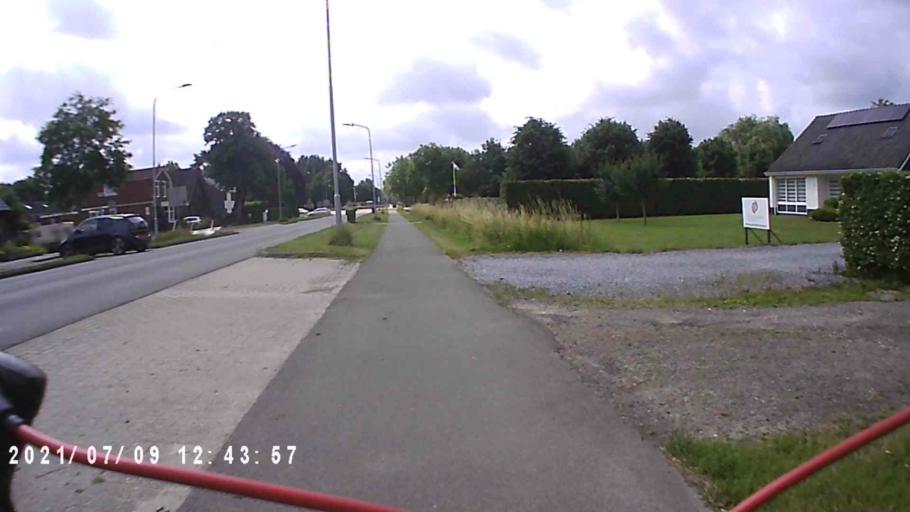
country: NL
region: Groningen
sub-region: Gemeente  Oldambt
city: Winschoten
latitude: 53.1343
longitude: 7.0227
